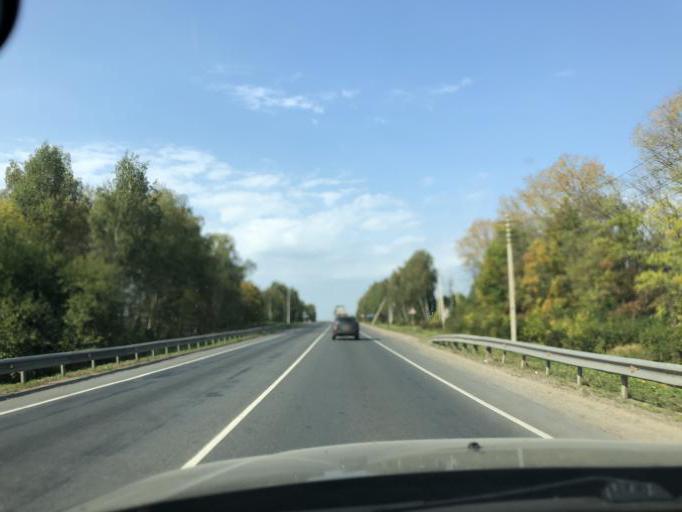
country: RU
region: Moskovskaya
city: L'vovskiy
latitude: 55.3335
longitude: 37.5040
